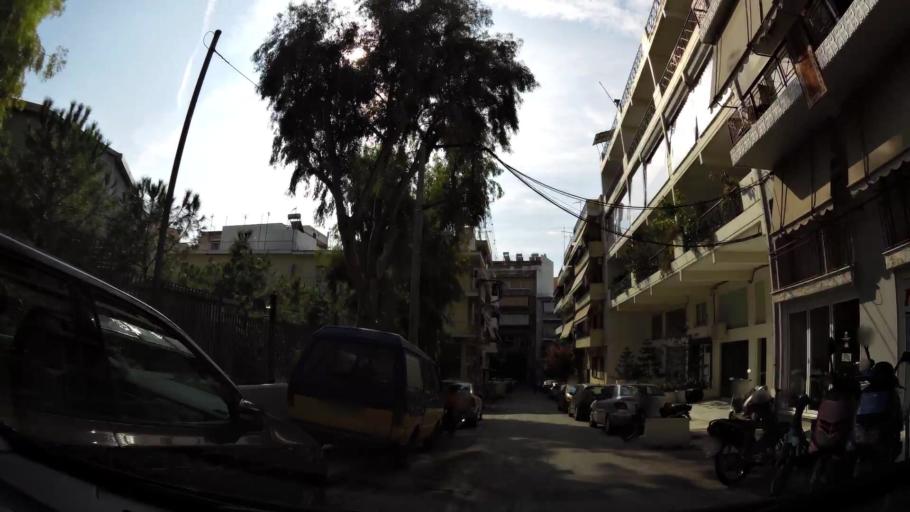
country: GR
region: Attica
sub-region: Nomarchia Athinas
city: Galatsi
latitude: 38.0154
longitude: 23.7492
